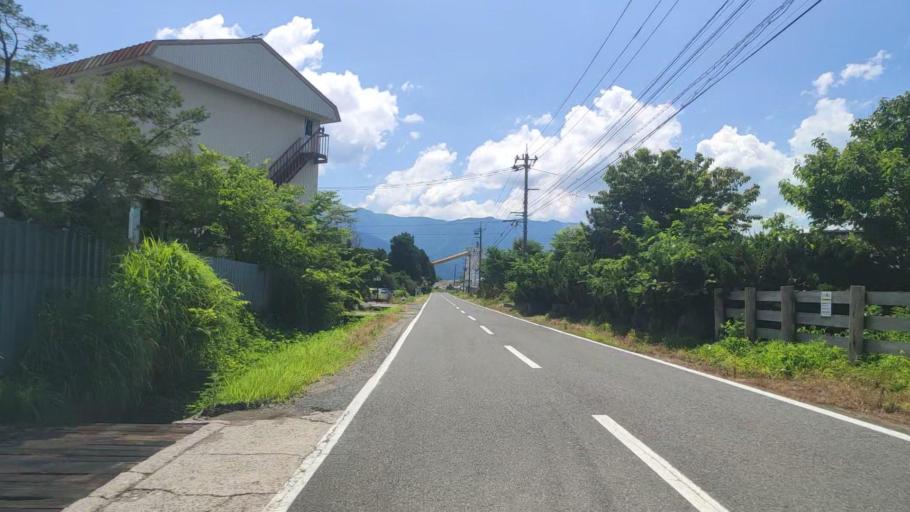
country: JP
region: Fukui
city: Ono
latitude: 35.9775
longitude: 136.5199
